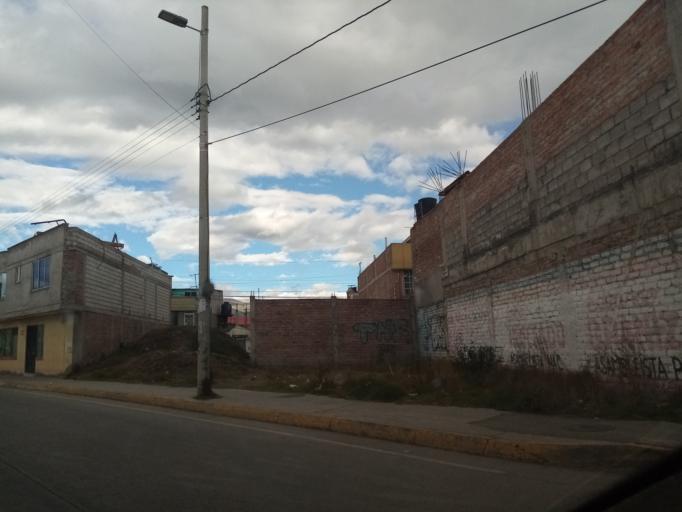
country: EC
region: Chimborazo
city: Riobamba
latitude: -1.6902
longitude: -78.6357
